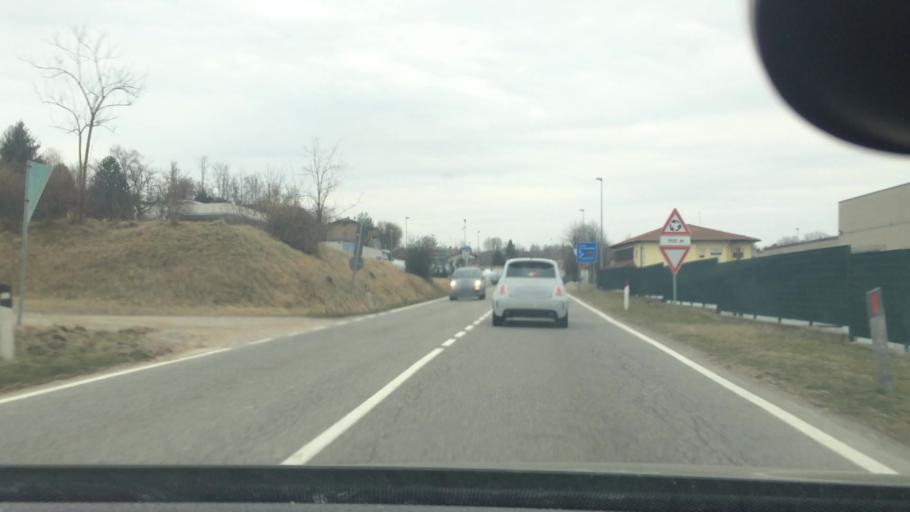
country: IT
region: Lombardy
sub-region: Provincia di Como
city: Lambrugo
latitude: 45.7670
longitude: 9.2292
